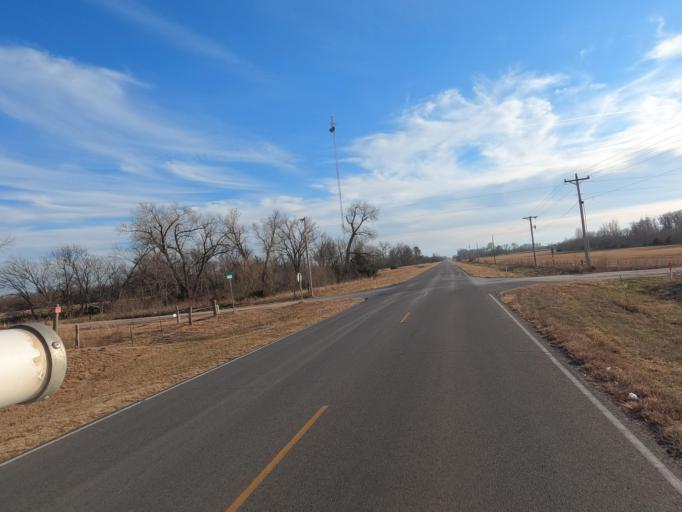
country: US
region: Kansas
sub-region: Reno County
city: Buhler
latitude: 38.1014
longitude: -97.7755
